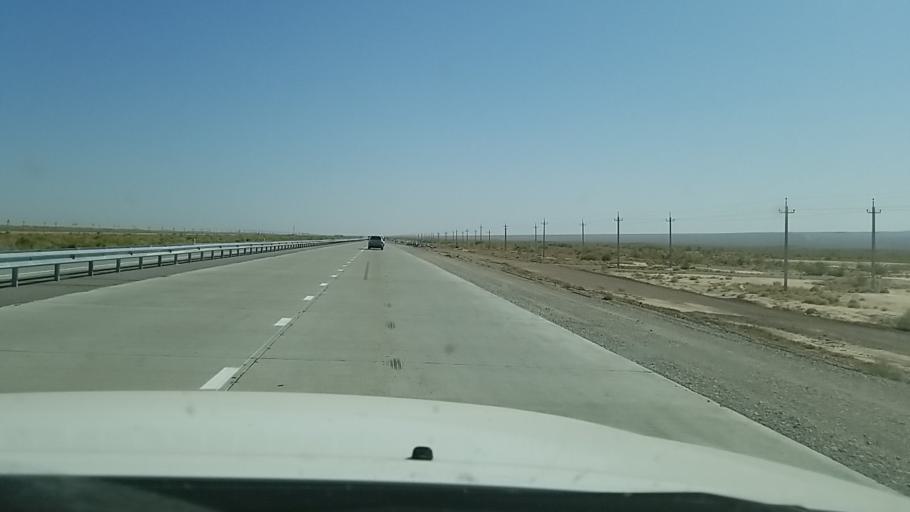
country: KZ
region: Almaty Oblysy
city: Kegen
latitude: 43.7451
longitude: 78.8531
